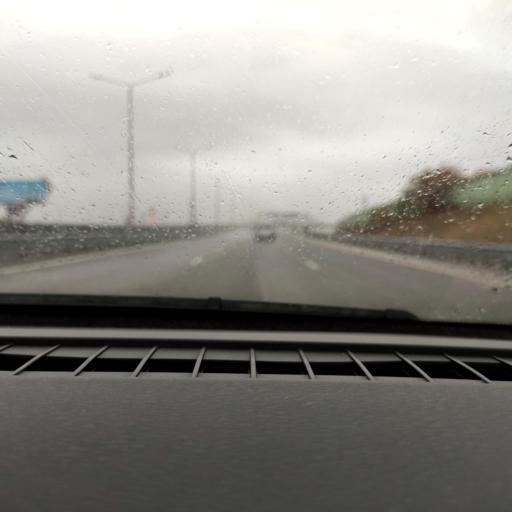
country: RU
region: Voronezj
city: Ramon'
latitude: 51.8264
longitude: 39.2478
